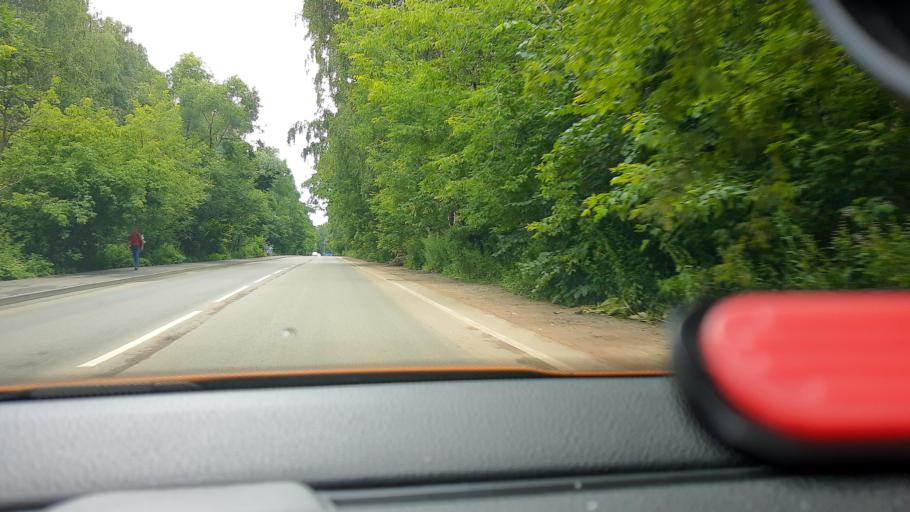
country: RU
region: Moskovskaya
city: Krasnogorsk
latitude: 55.8694
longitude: 37.3457
